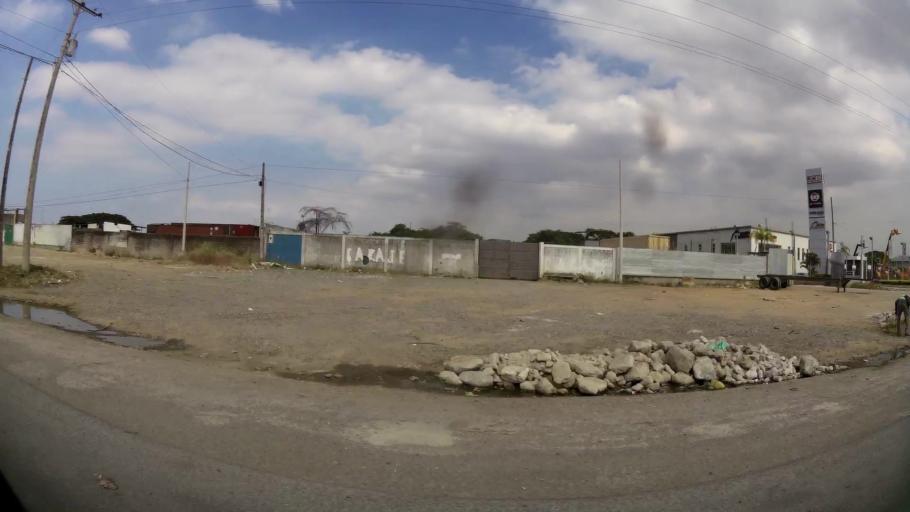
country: EC
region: Guayas
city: Santa Lucia
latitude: -2.0844
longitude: -79.9432
